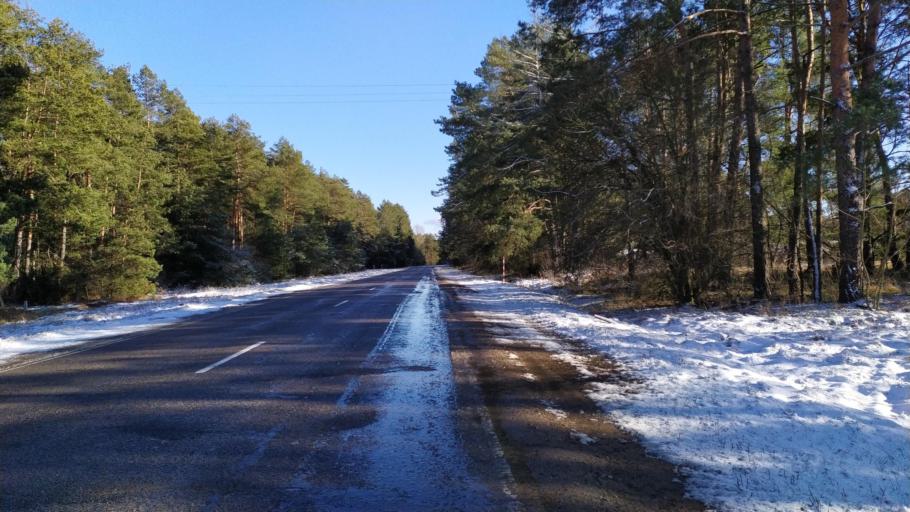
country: BY
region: Brest
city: Kamyanyets
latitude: 52.3858
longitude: 23.8517
